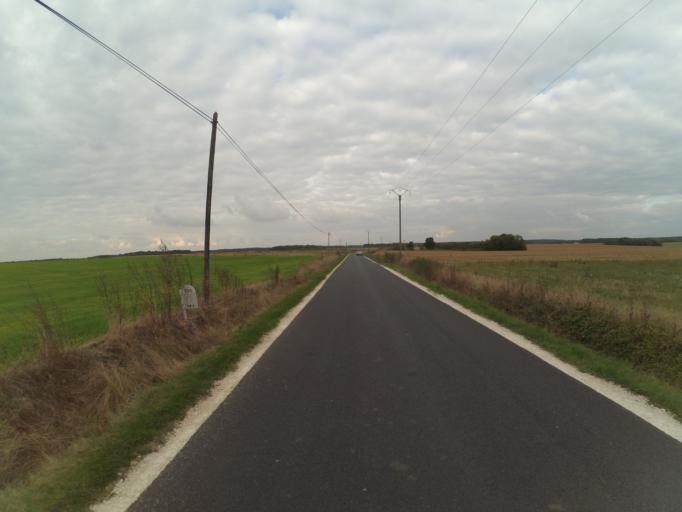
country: FR
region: Centre
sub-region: Departement d'Indre-et-Loire
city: Nazelles-Negron
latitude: 47.4914
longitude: 0.9574
